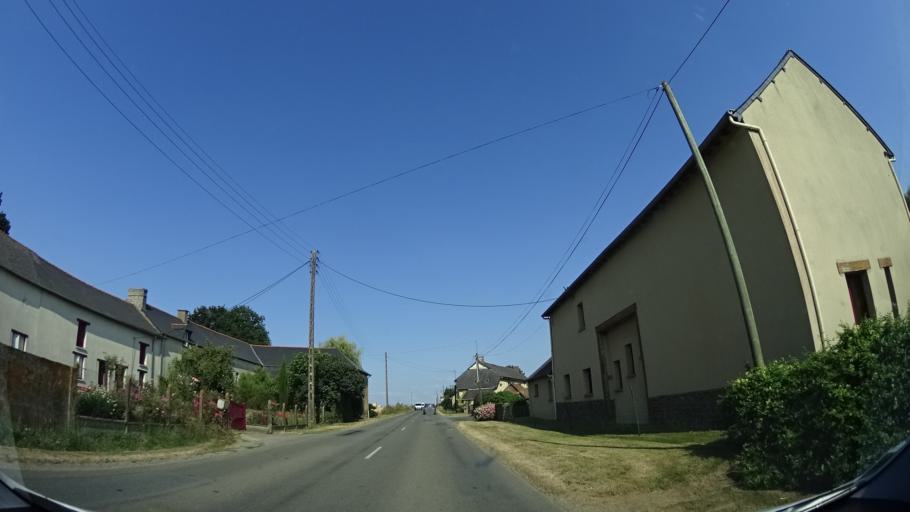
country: FR
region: Brittany
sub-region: Departement d'Ille-et-Vilaine
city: Romille
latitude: 48.2166
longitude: -1.8688
